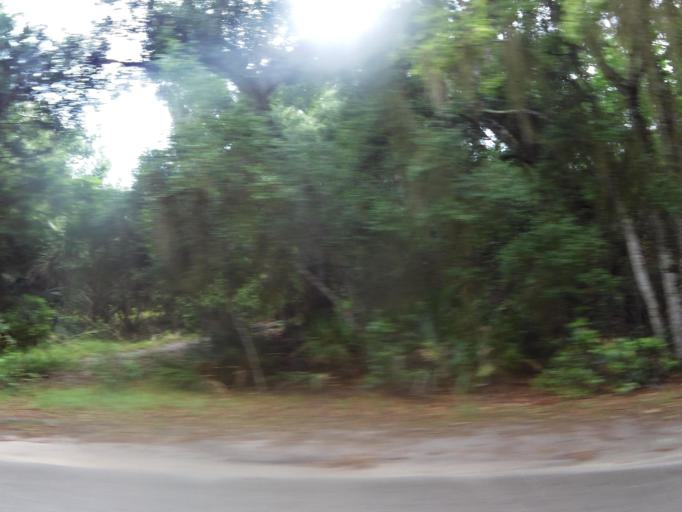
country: US
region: Florida
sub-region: Nassau County
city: Fernandina Beach
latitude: 30.6974
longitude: -81.4413
